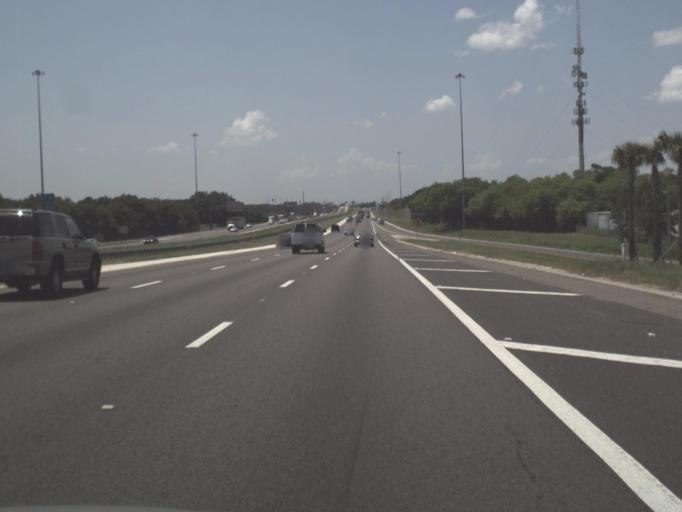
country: US
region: Florida
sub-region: Hillsborough County
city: East Lake-Orient Park
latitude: 27.9806
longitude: -82.3857
